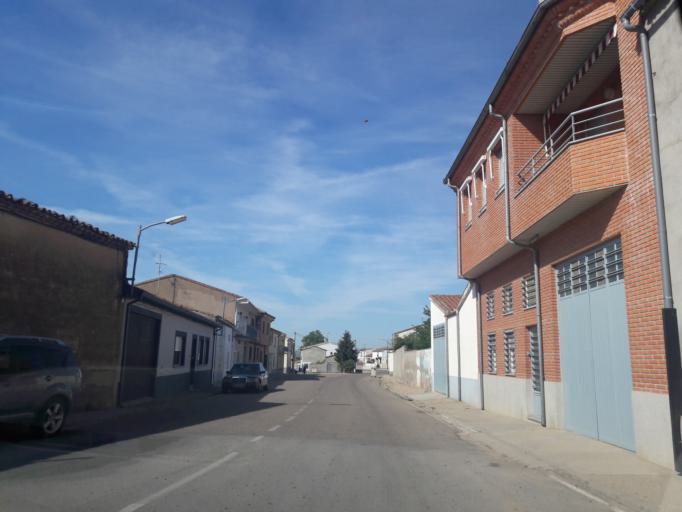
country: ES
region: Castille and Leon
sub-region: Provincia de Salamanca
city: Villoruela
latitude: 41.0073
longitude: -5.3950
